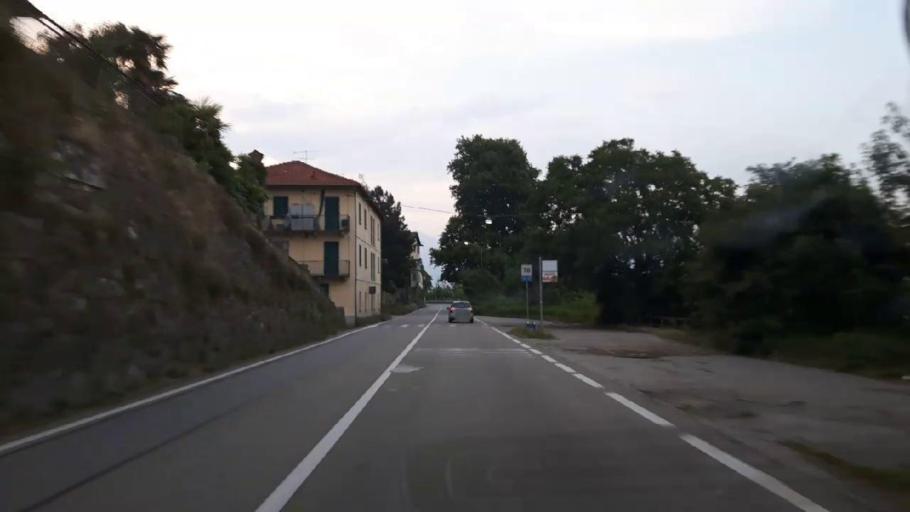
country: IT
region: Piedmont
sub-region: Provincia Verbano-Cusio-Ossola
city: Belgirate
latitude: 45.8627
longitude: 8.5674
